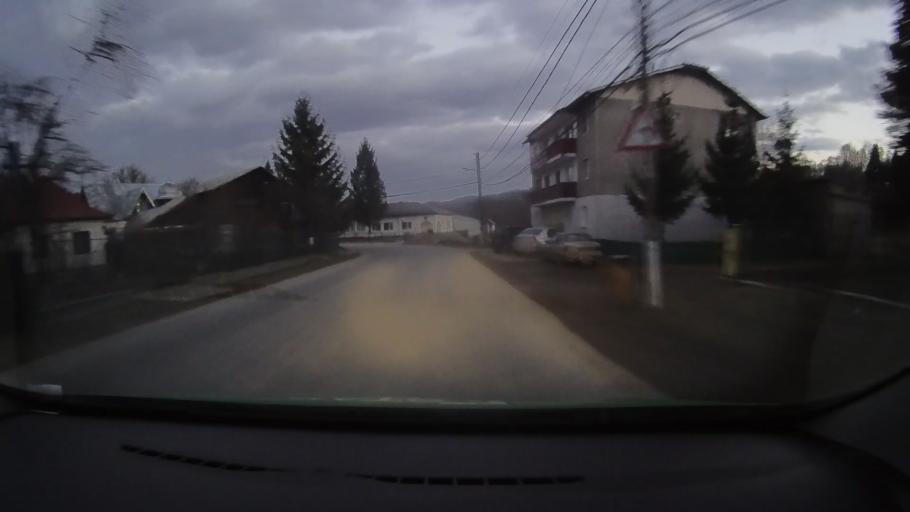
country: RO
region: Prahova
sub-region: Comuna Provita de Sus
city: Provita de Sus
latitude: 45.1360
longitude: 25.6358
